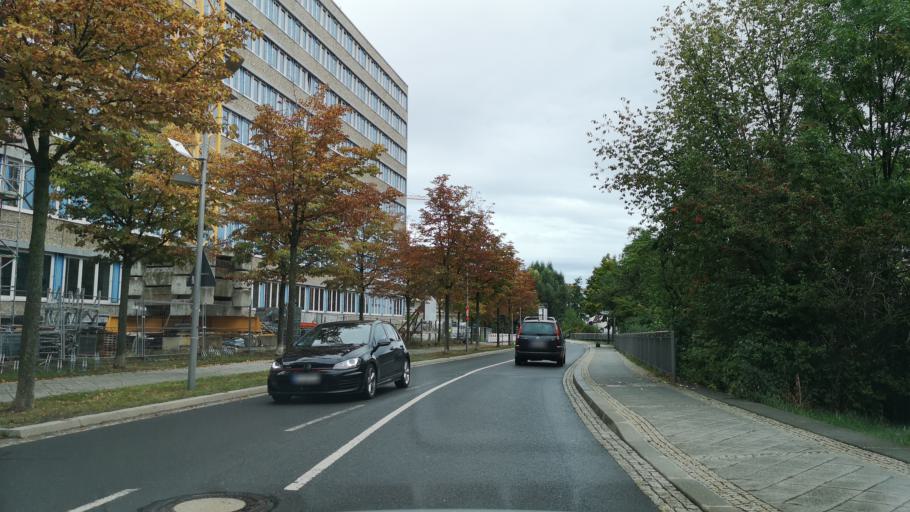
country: DE
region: Thuringia
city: Erfurt
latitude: 50.9717
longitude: 11.0143
